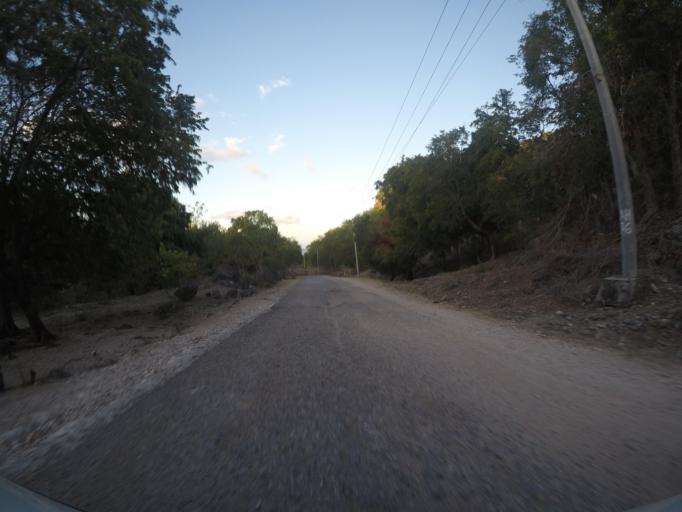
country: TL
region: Lautem
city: Lospalos
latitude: -8.3439
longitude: 127.0342
